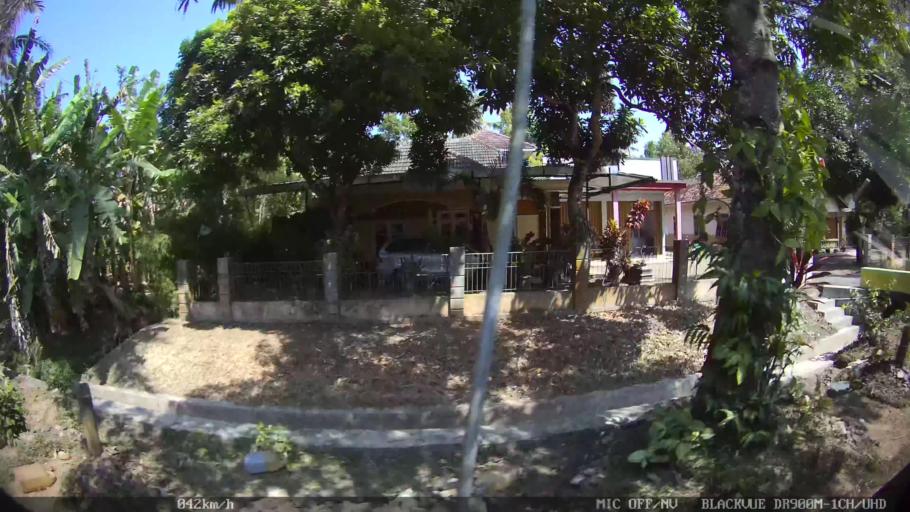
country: ID
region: Daerah Istimewa Yogyakarta
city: Srandakan
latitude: -7.9073
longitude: 110.1521
